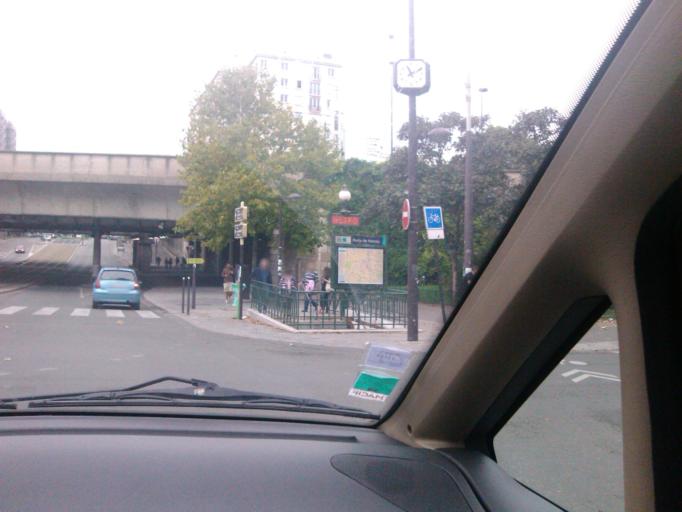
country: FR
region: Ile-de-France
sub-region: Departement des Hauts-de-Seine
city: Malakoff
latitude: 48.8278
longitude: 2.3057
